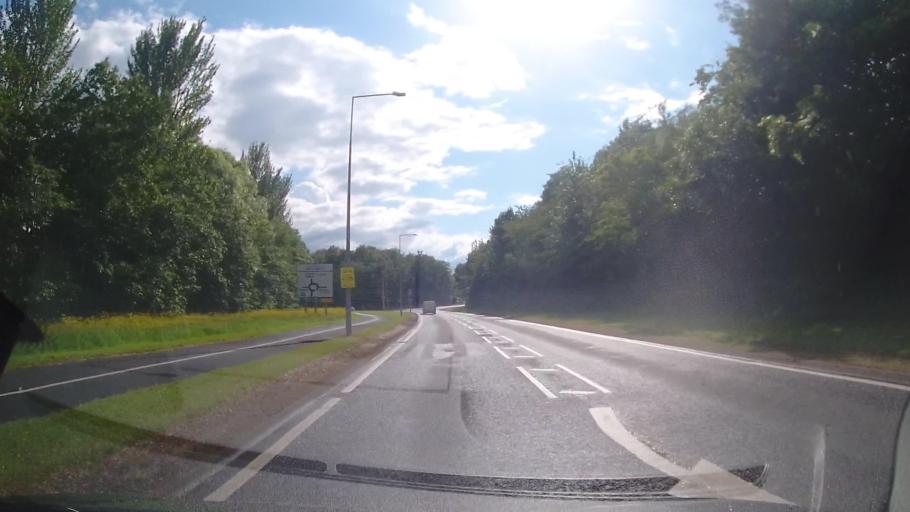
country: GB
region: England
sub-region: Telford and Wrekin
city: Telford
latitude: 52.6676
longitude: -2.4710
